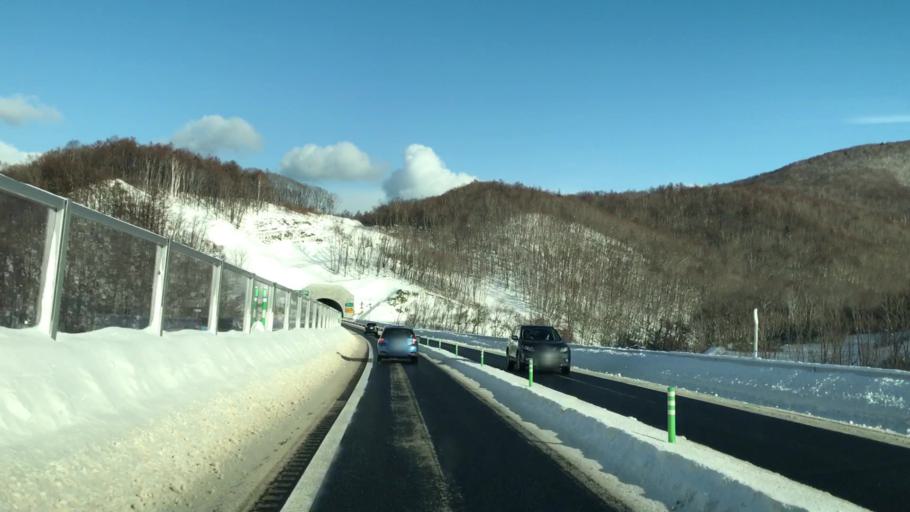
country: JP
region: Hokkaido
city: Otaru
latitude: 43.1535
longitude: 141.0435
